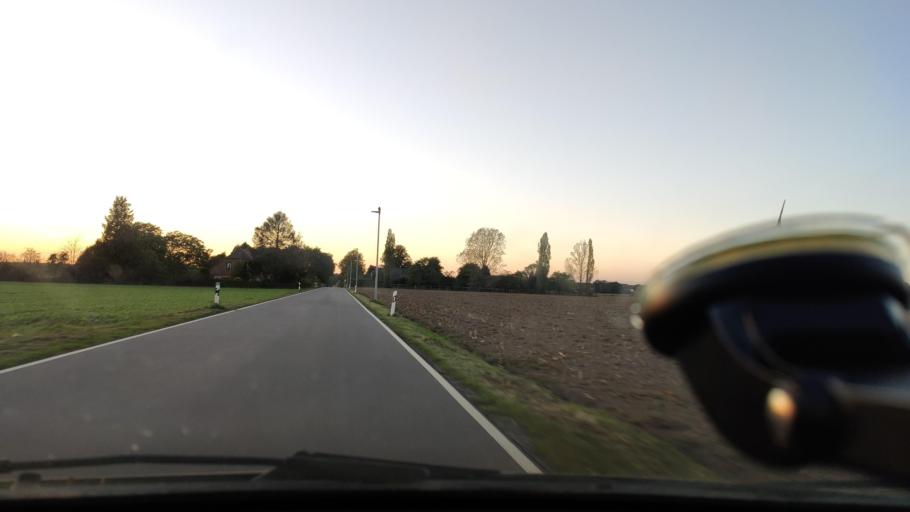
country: DE
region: North Rhine-Westphalia
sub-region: Regierungsbezirk Dusseldorf
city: Goch
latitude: 51.7182
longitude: 6.2061
